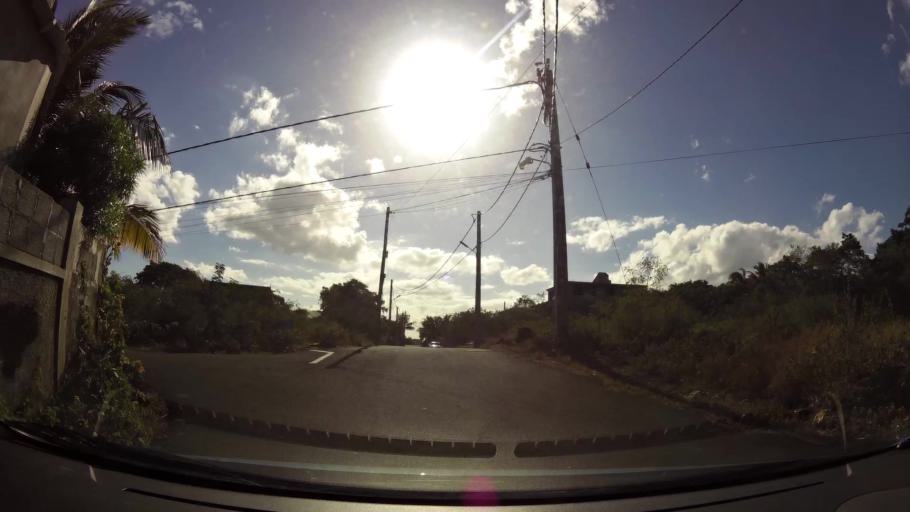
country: MU
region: Black River
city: Albion
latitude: -20.2004
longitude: 57.4078
